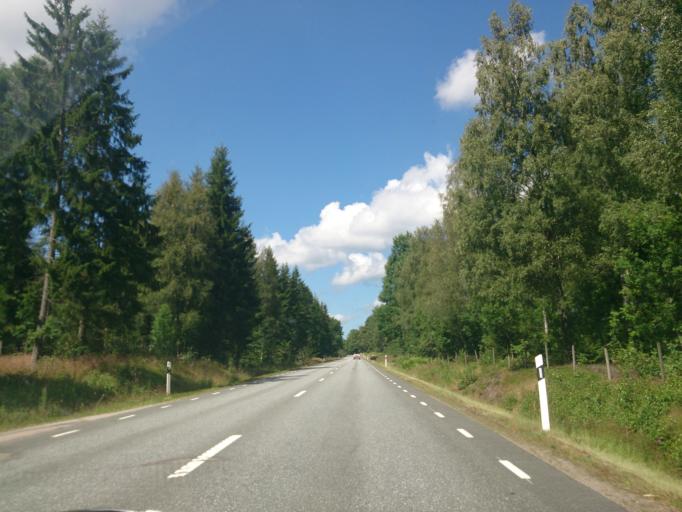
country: SE
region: Halland
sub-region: Hylte Kommun
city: Hyltebruk
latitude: 57.1378
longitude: 13.2011
